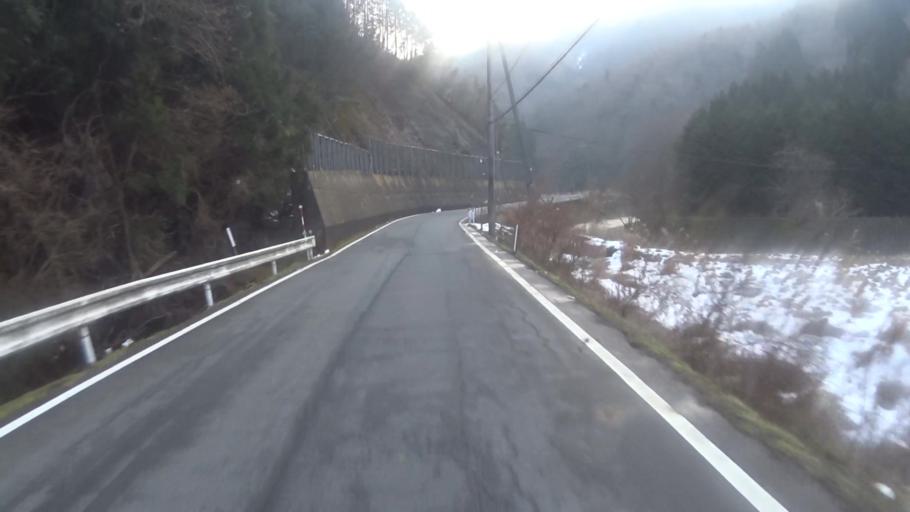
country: JP
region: Kyoto
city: Maizuru
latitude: 35.4123
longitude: 135.4621
